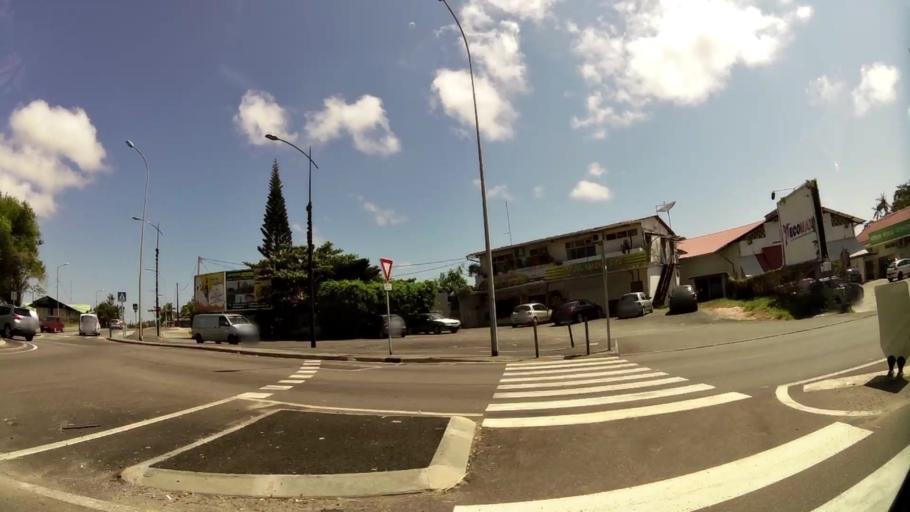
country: GF
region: Guyane
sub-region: Guyane
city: Cayenne
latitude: 4.9206
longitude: -52.3217
